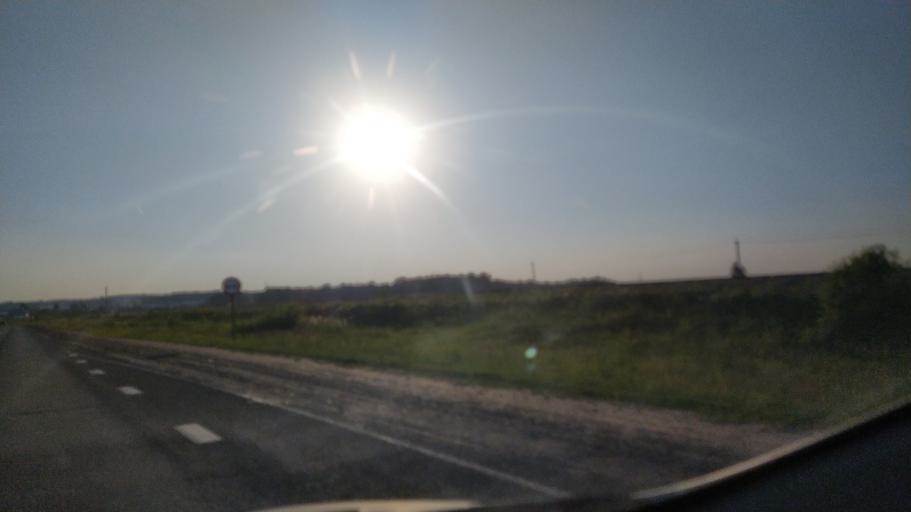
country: RU
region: Chuvashia
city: Kugesi
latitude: 56.0408
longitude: 47.3305
